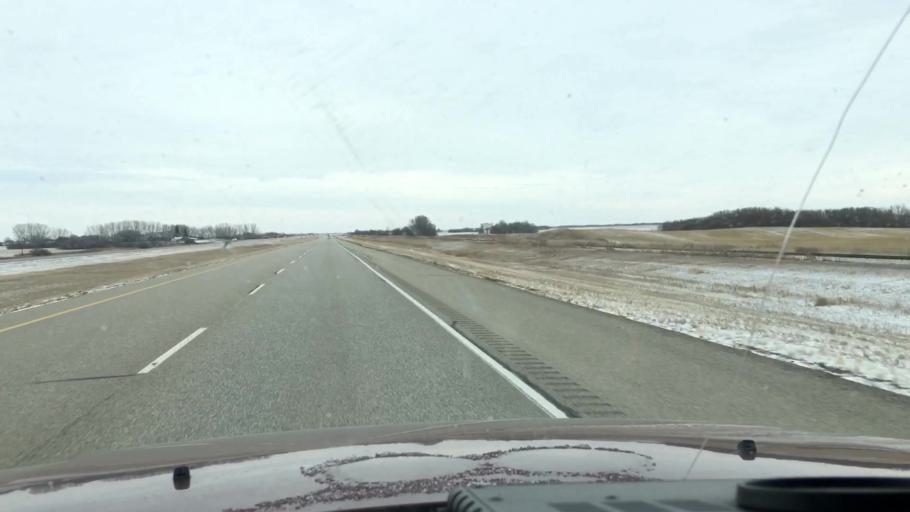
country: CA
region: Saskatchewan
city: Watrous
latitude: 51.3466
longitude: -106.1097
